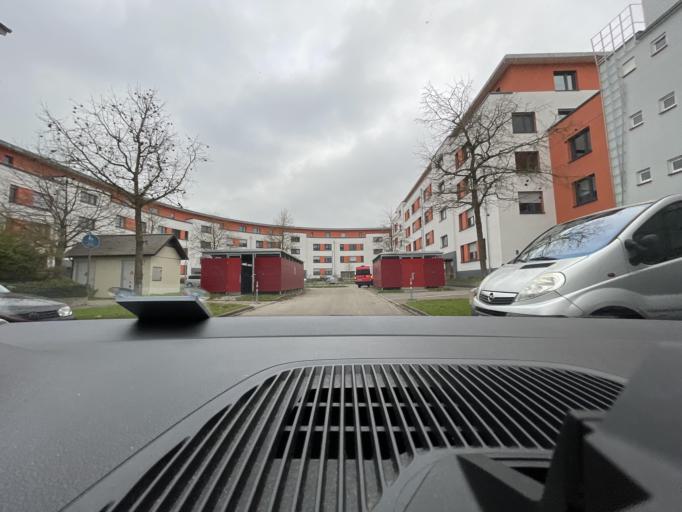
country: DE
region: Baden-Wuerttemberg
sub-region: Karlsruhe Region
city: Karlsruhe
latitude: 48.9797
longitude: 8.3681
